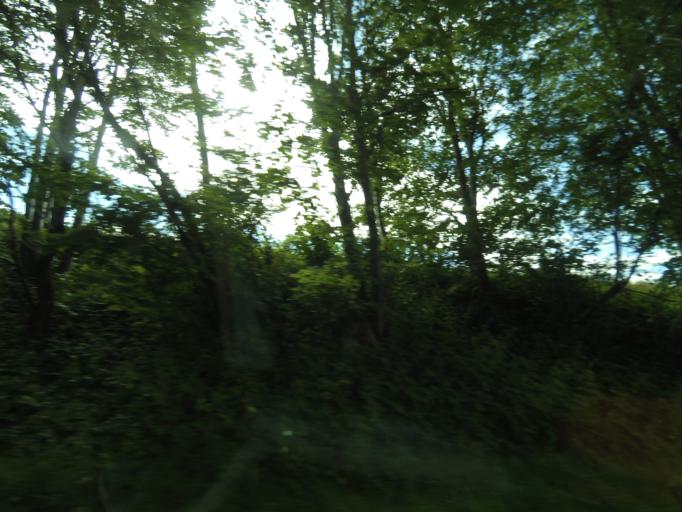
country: DK
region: South Denmark
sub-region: Assens Kommune
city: Vissenbjerg
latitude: 55.4359
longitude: 10.1835
